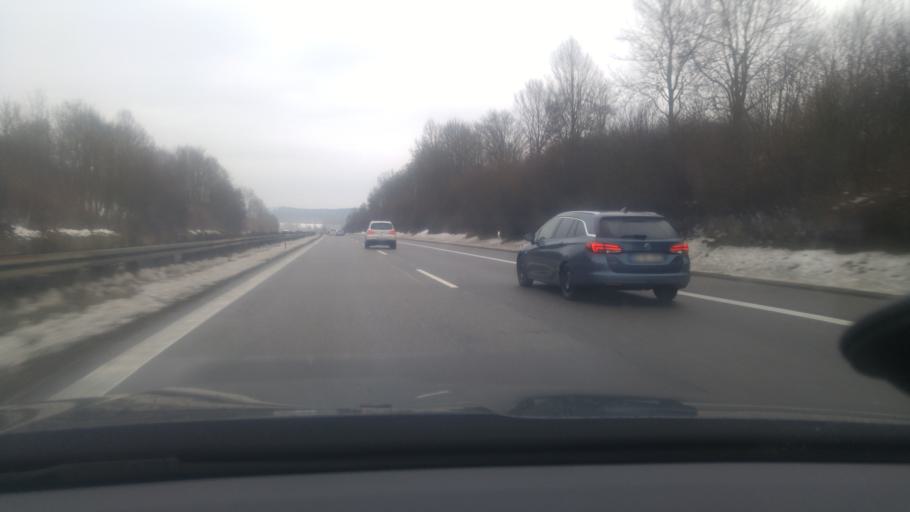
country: DE
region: Baden-Wuerttemberg
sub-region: Freiburg Region
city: Deisslingen
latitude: 48.1105
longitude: 8.5824
